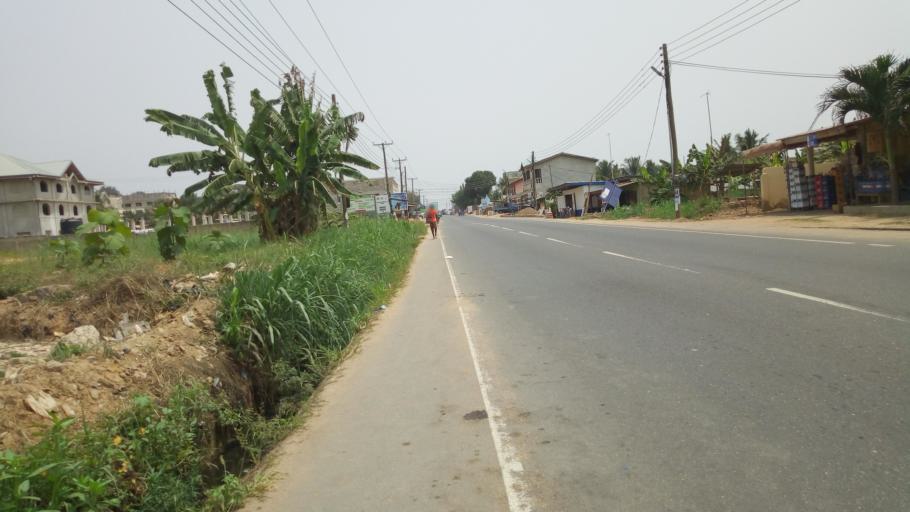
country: GH
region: Greater Accra
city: Gbawe
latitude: 5.5576
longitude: -0.3070
